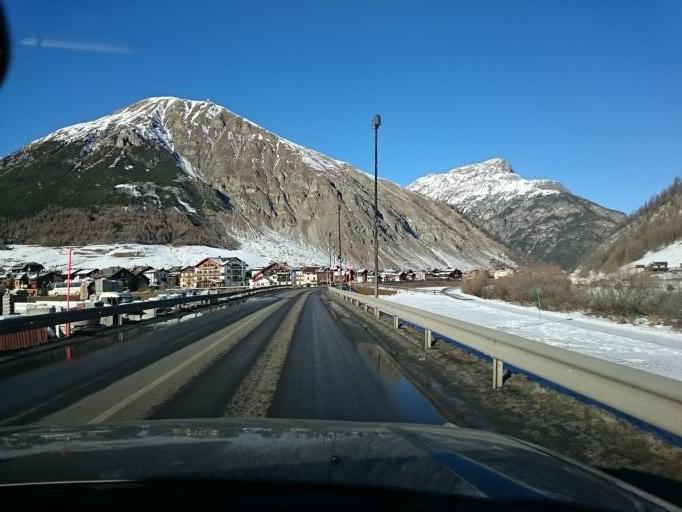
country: IT
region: Lombardy
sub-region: Provincia di Sondrio
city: Livigno
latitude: 46.5467
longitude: 10.1425
